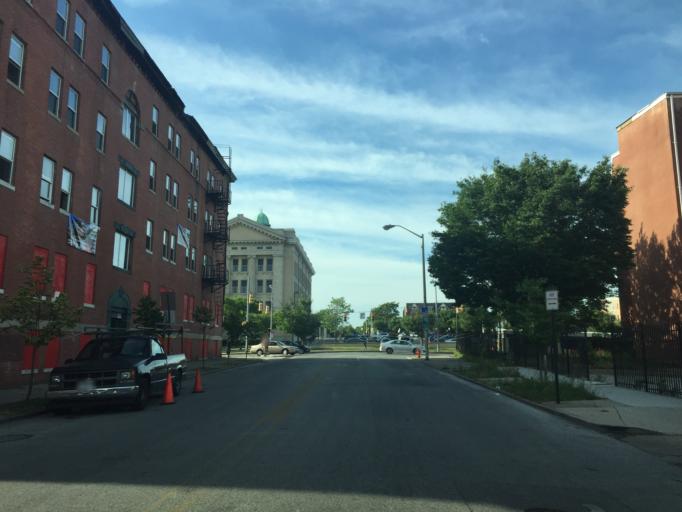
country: US
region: Maryland
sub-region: City of Baltimore
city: Baltimore
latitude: 39.3106
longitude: -76.6124
